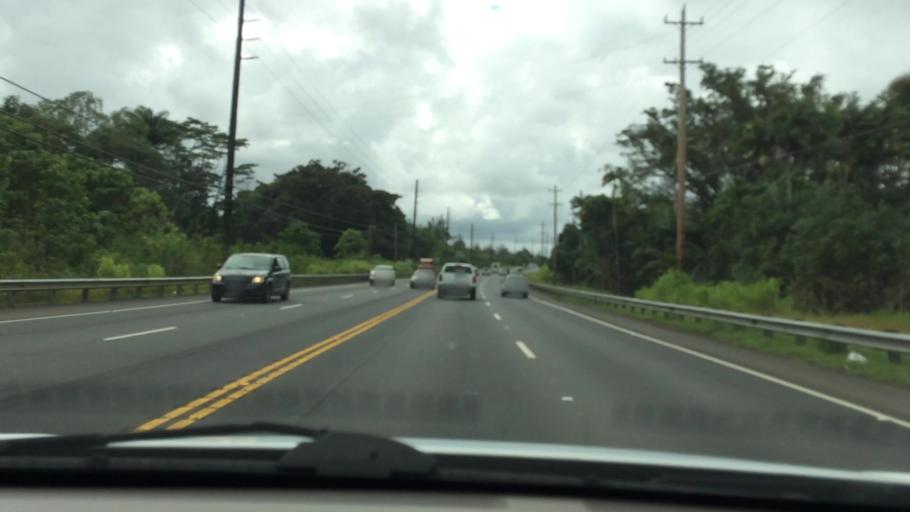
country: US
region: Hawaii
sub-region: Hawaii County
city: Orchidlands Estates
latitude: 19.5877
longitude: -155.0127
